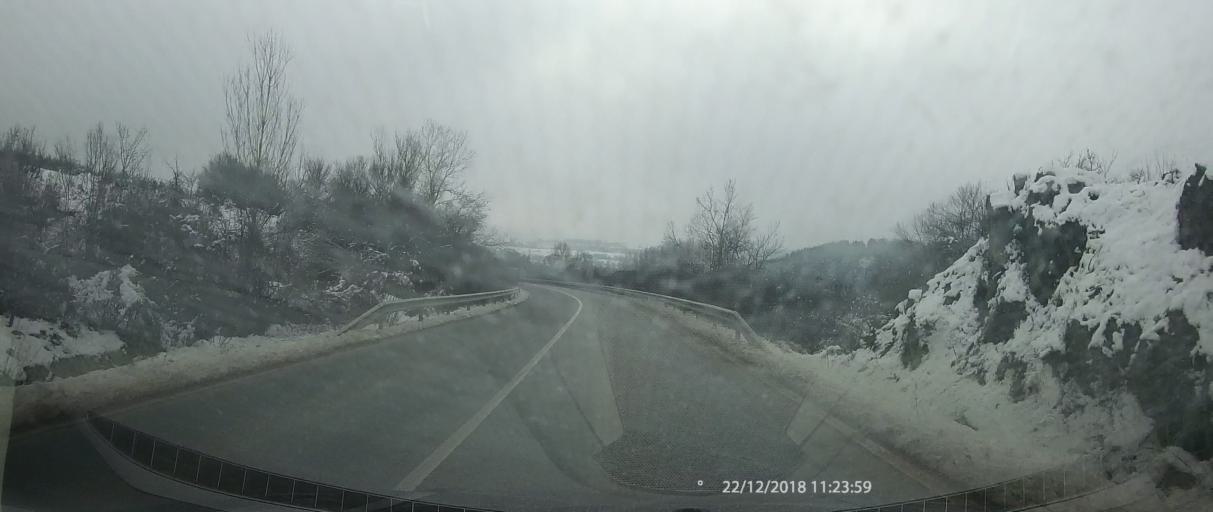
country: BG
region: Kyustendil
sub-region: Obshtina Boboshevo
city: Boboshevo
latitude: 42.2536
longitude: 22.8861
